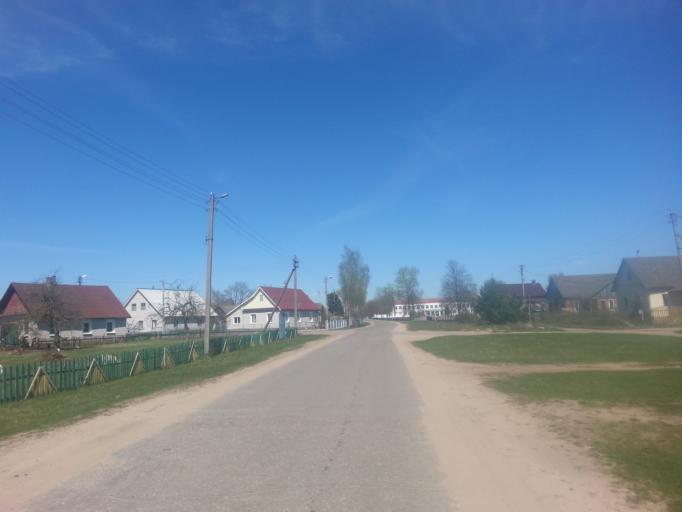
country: BY
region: Minsk
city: Narach
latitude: 54.9280
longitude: 26.6814
